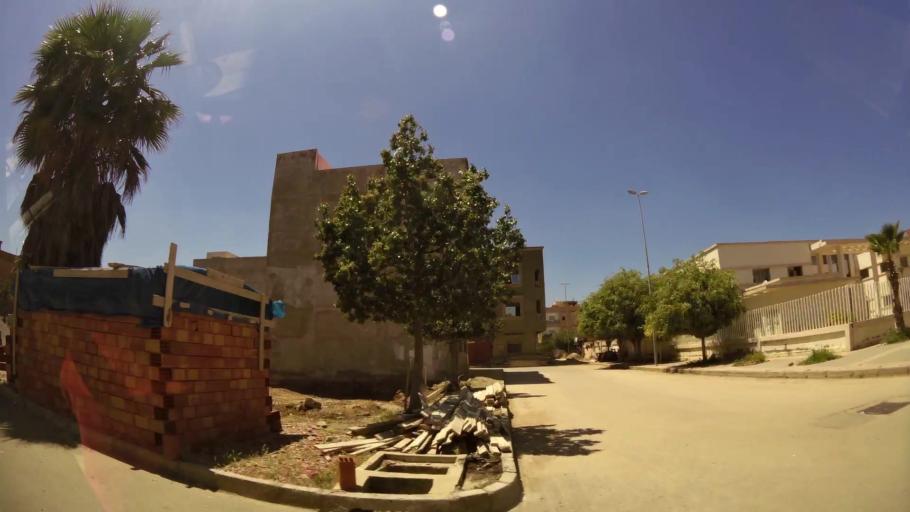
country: MA
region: Oriental
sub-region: Berkane-Taourirt
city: Madagh
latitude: 35.0748
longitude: -2.2243
